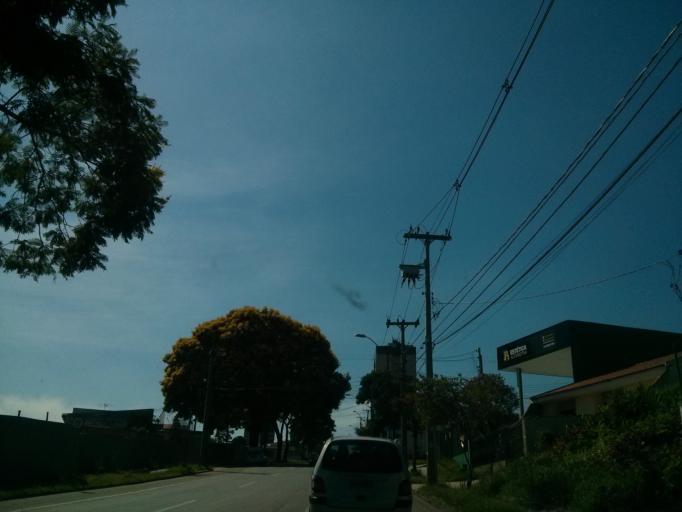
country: BR
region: Parana
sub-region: Sao Jose Dos Pinhais
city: Sao Jose dos Pinhais
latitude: -25.5314
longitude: -49.2135
